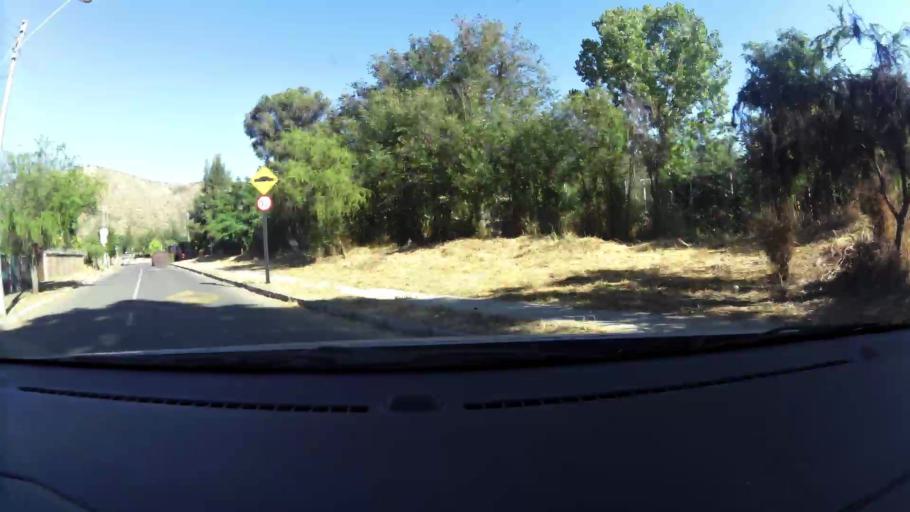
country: CL
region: Santiago Metropolitan
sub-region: Provincia de Chacabuco
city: Lampa
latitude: -33.3962
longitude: -71.1221
